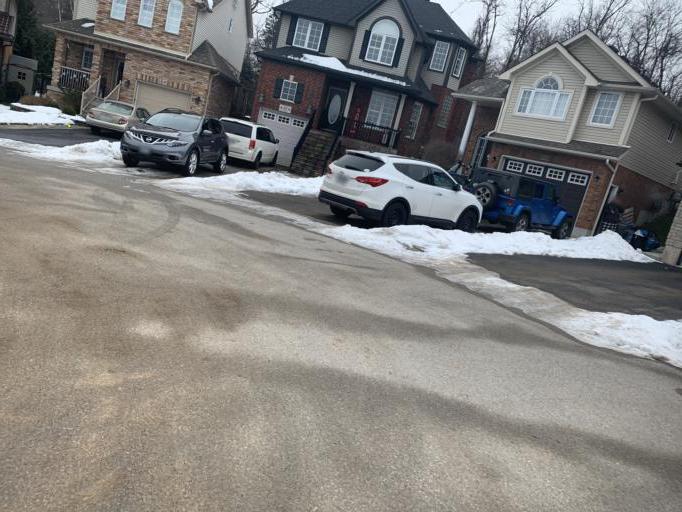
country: CA
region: Ontario
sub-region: Halton
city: Milton
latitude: 43.6587
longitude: -79.9205
